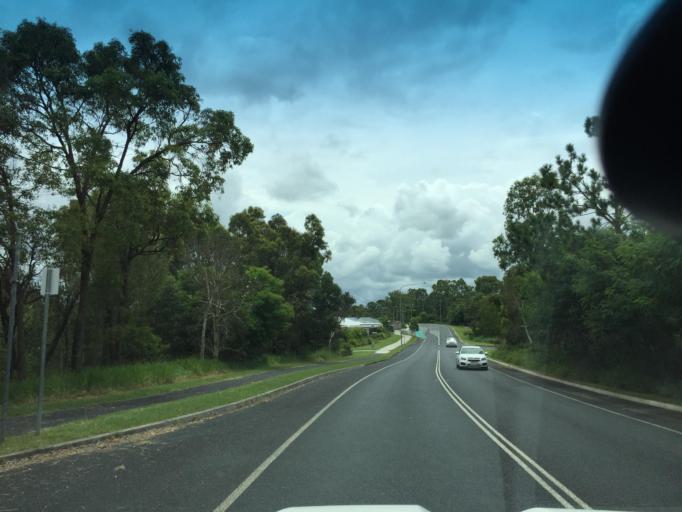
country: AU
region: Queensland
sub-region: Moreton Bay
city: Caboolture
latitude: -27.0666
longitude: 152.9330
